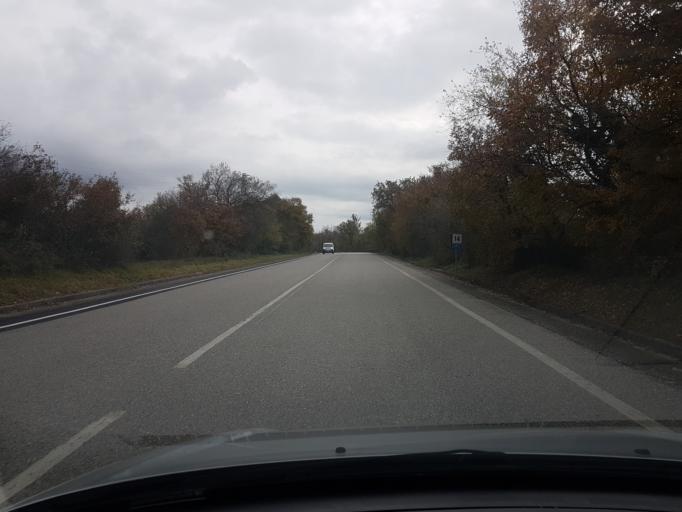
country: IT
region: Friuli Venezia Giulia
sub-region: Provincia di Trieste
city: Villa Opicina
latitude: 45.6985
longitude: 13.7721
